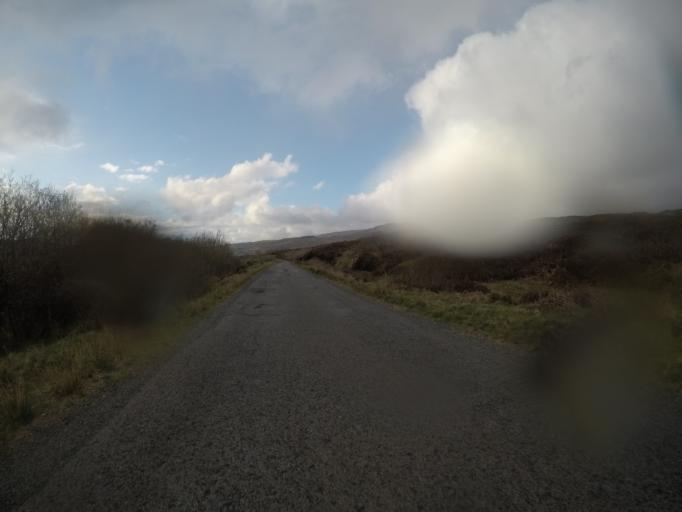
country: GB
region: Scotland
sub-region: Highland
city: Isle of Skye
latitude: 57.4674
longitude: -6.2987
